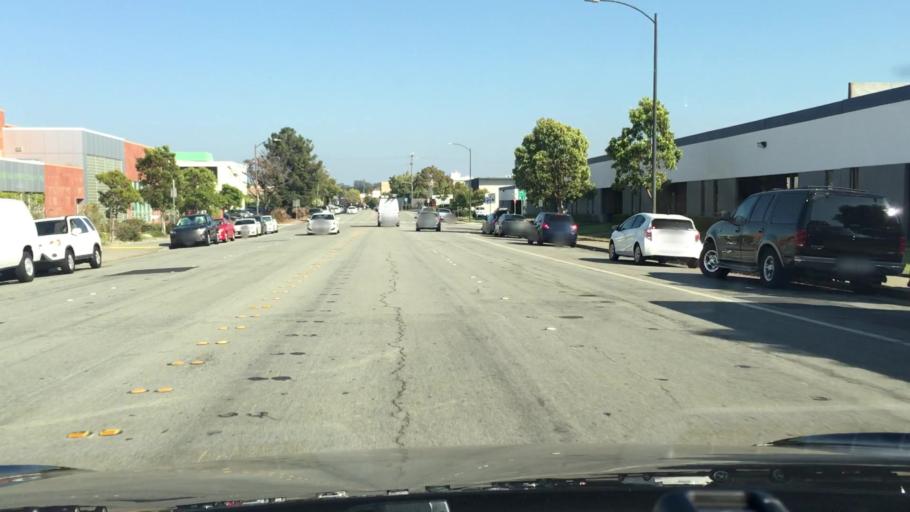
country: US
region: California
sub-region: San Mateo County
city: Burlingame
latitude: 37.5925
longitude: -122.3695
